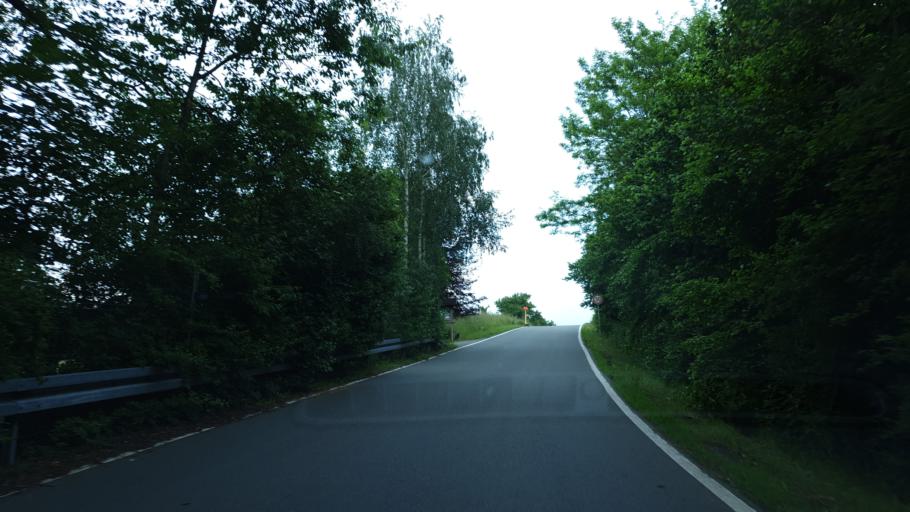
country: DE
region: Saxony
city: Oberlungwitz
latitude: 50.7931
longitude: 12.6872
